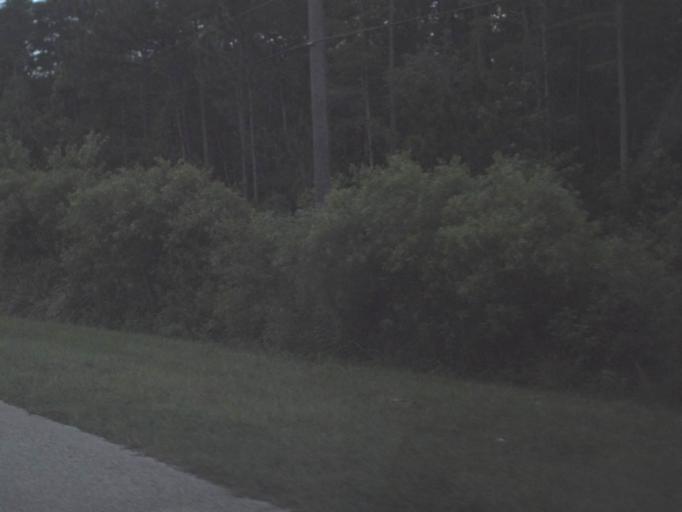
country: US
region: Florida
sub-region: Saint Johns County
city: Palm Valley
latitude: 30.0600
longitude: -81.4347
